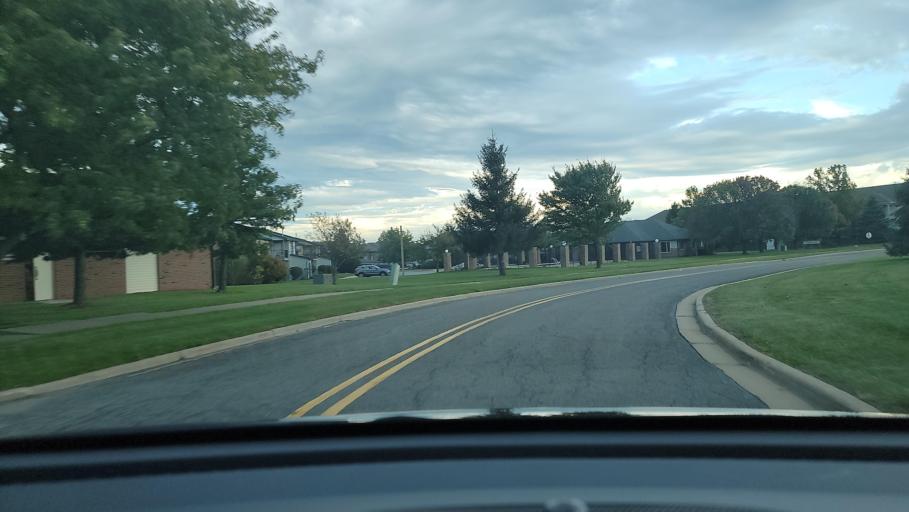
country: US
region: Indiana
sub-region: Porter County
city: South Haven
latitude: 41.5544
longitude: -87.1588
